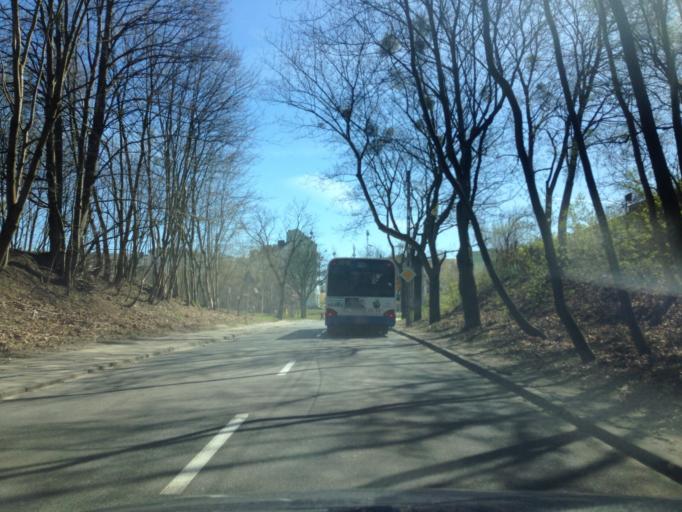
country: PL
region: Pomeranian Voivodeship
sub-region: Gdynia
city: Gdynia
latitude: 54.5029
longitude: 18.5141
